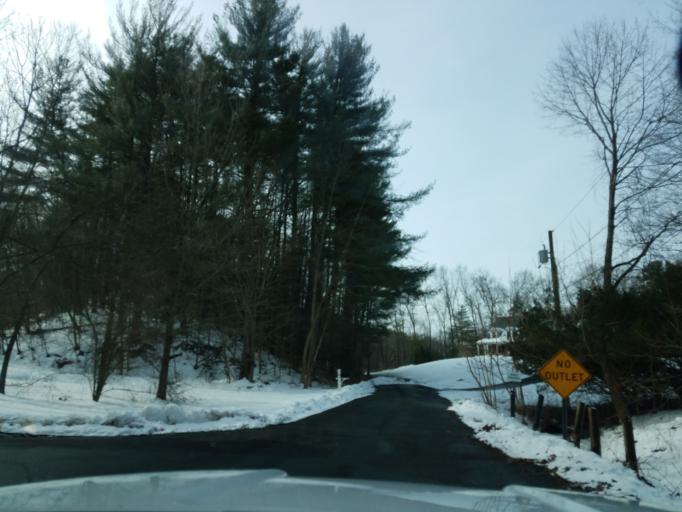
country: US
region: Connecticut
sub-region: Hartford County
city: Weatogue
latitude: 41.7960
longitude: -72.8189
